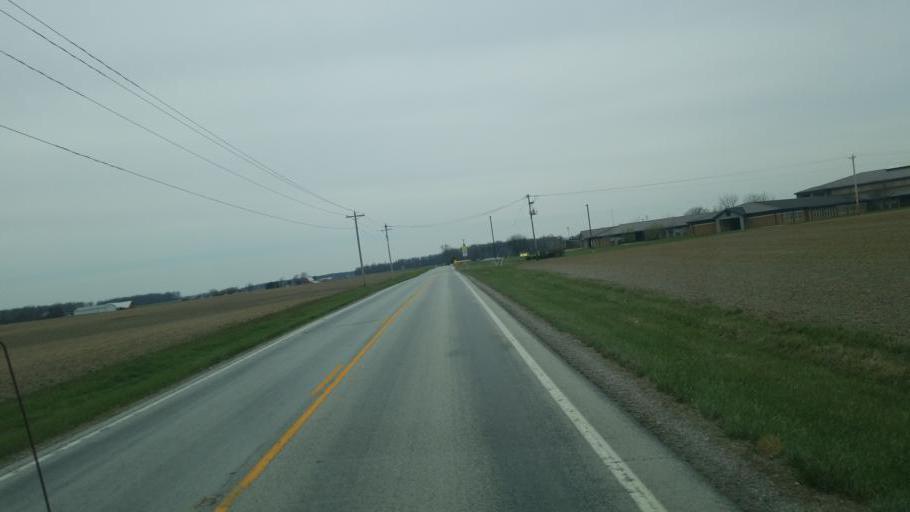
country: US
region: Ohio
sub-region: Hardin County
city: Forest
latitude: 40.8641
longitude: -83.5201
